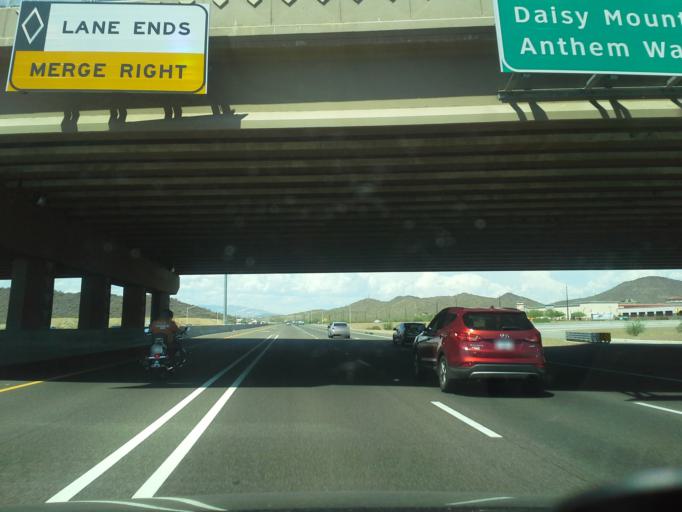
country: US
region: Arizona
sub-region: Maricopa County
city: Anthem
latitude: 33.7979
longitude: -112.1353
